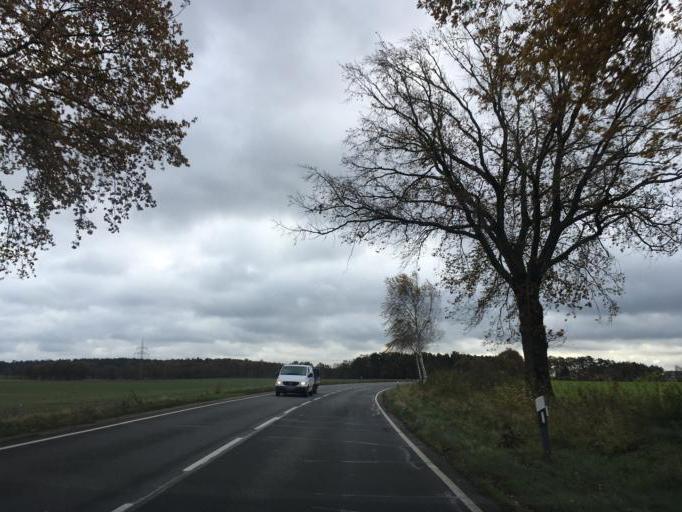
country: DE
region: Lower Saxony
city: Deutsch Evern
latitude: 53.2103
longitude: 10.4452
